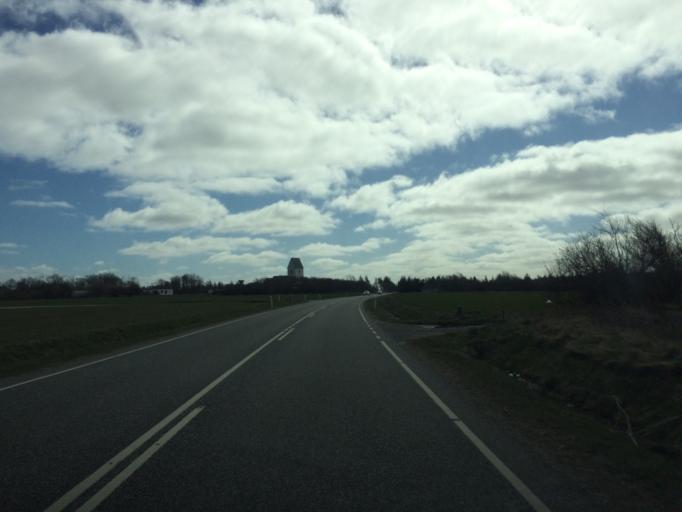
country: DK
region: Central Jutland
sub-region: Holstebro Kommune
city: Ulfborg
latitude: 56.3087
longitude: 8.1802
